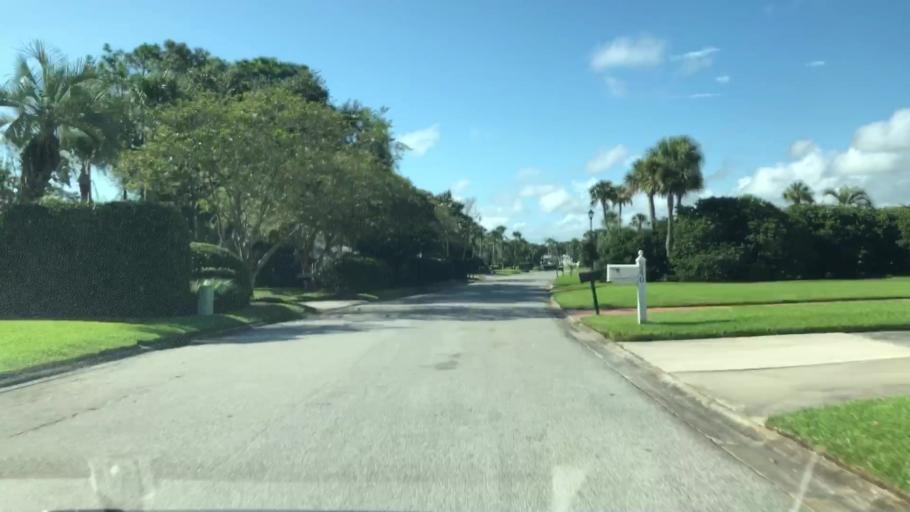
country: US
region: Florida
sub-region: Saint Johns County
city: Ponte Vedra Beach
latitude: 30.2377
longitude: -81.3842
